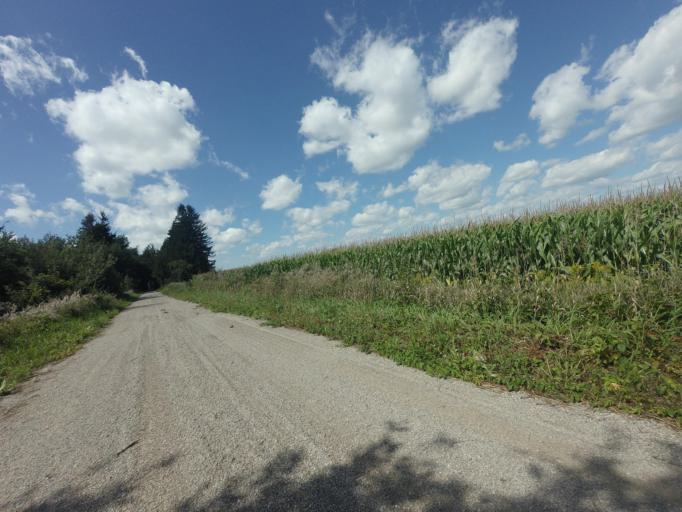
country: CA
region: Ontario
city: Huron East
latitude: 43.6573
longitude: -81.2440
